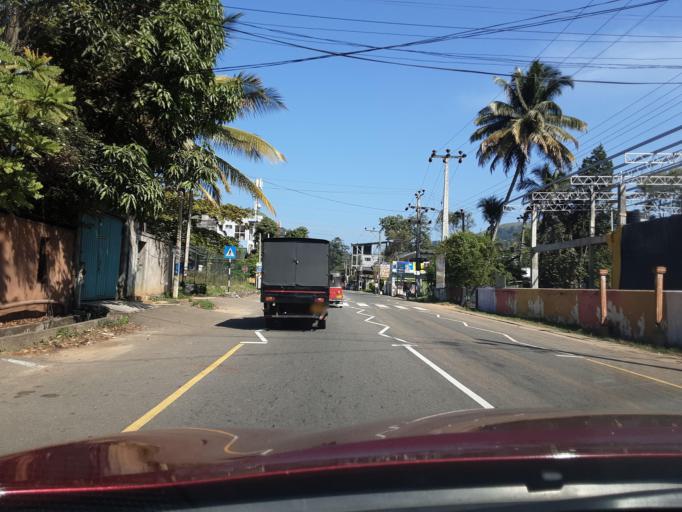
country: LK
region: Uva
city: Badulla
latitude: 6.9965
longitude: 81.0573
